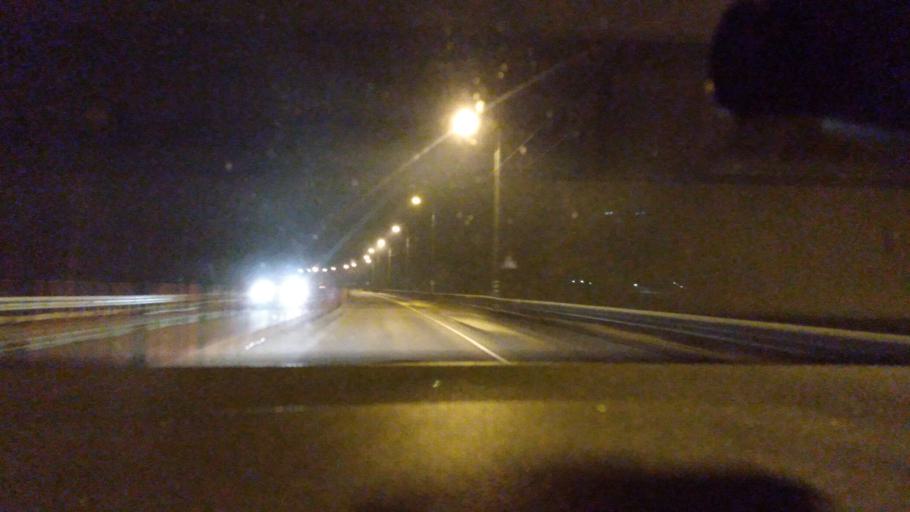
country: RU
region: Moskovskaya
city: Il'inskiy Pogost
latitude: 55.4850
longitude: 38.9231
